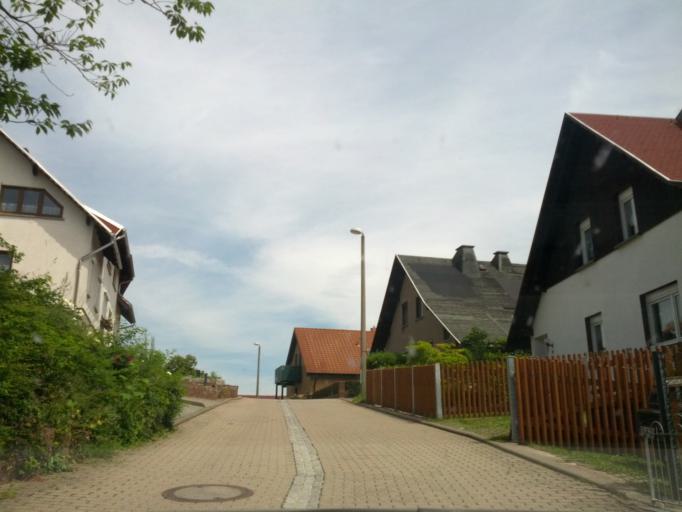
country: DE
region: Thuringia
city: Finsterbergen
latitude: 50.8350
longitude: 10.5839
